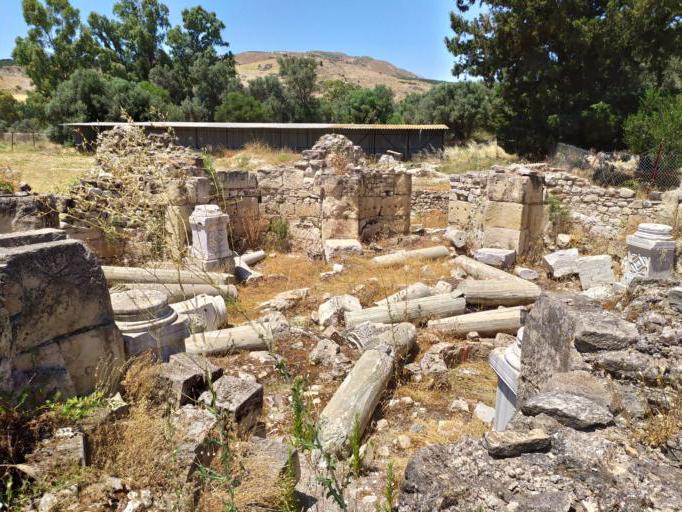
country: GR
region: Crete
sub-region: Nomos Irakleiou
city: Agioi Deka
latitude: 35.0591
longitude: 24.9463
